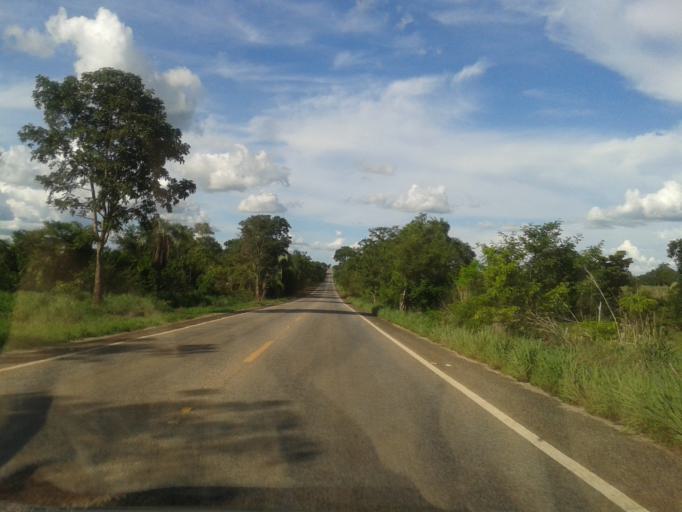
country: BR
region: Goias
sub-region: Mozarlandia
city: Mozarlandia
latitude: -14.5439
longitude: -50.4908
